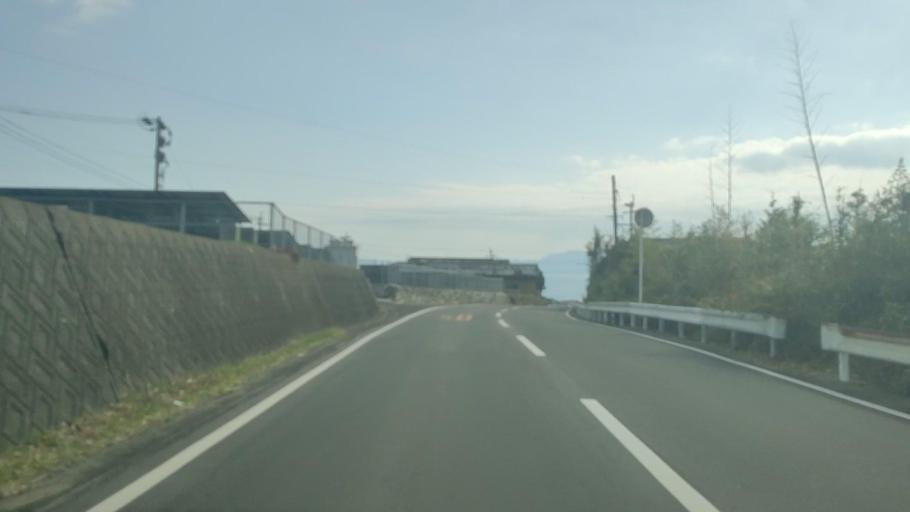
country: JP
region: Nagasaki
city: Shimabara
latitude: 32.6635
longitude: 130.2872
